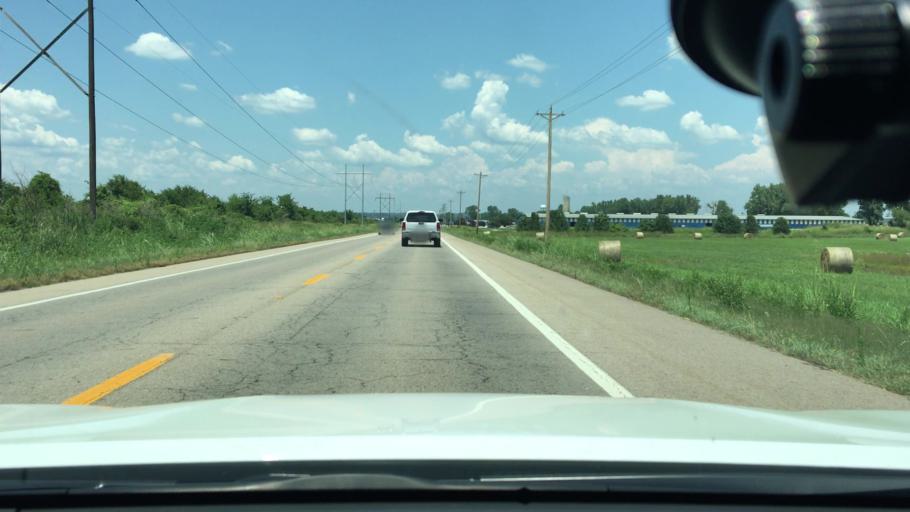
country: US
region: Arkansas
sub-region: Crawford County
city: Van Buren
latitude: 35.4017
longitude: -94.3301
